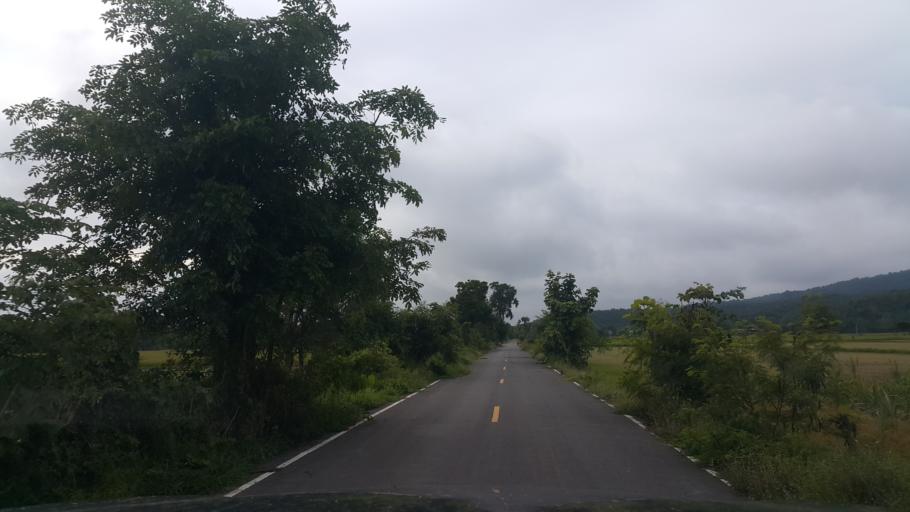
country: TH
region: Sukhothai
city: Sawankhalok
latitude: 17.3097
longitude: 99.6992
